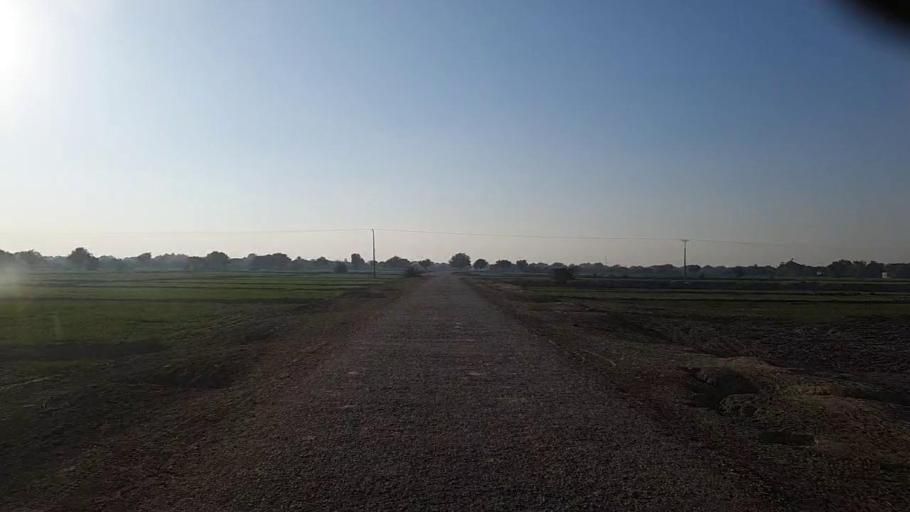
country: PK
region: Sindh
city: Pad Idan
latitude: 26.7341
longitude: 68.3485
